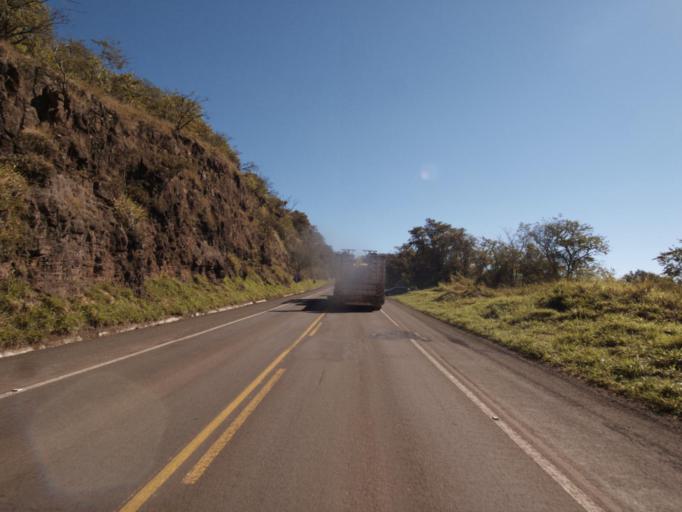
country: BR
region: Rio Grande do Sul
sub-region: Frederico Westphalen
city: Frederico Westphalen
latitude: -26.8154
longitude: -53.4313
